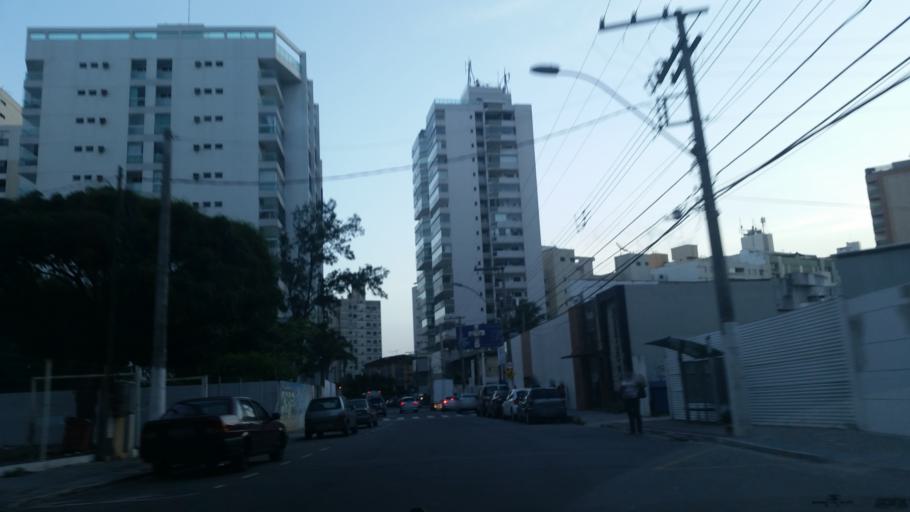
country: BR
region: Espirito Santo
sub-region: Vila Velha
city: Vila Velha
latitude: -20.3292
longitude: -40.2745
